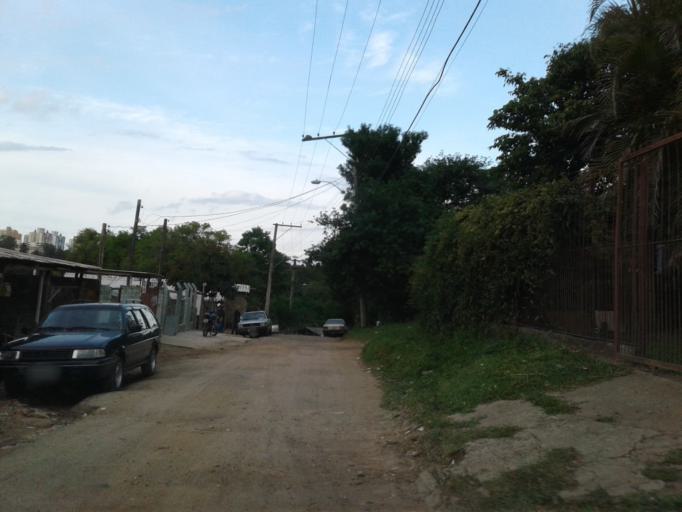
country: BR
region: Rio Grande do Sul
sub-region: Porto Alegre
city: Porto Alegre
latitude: -30.0538
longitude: -51.1409
